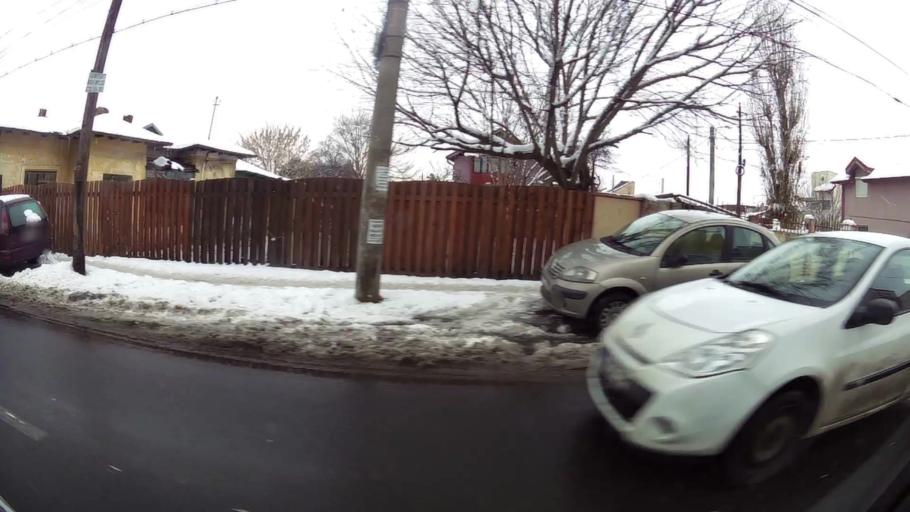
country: RO
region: Bucuresti
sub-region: Municipiul Bucuresti
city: Bucuresti
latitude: 44.3956
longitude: 26.1047
